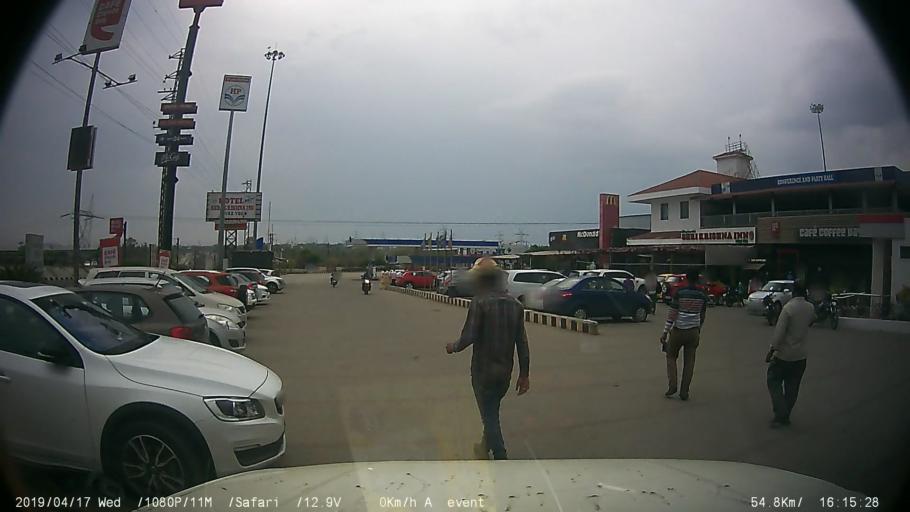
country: IN
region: Tamil Nadu
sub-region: Krishnagiri
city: Kelamangalam
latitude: 12.6657
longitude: 78.0038
